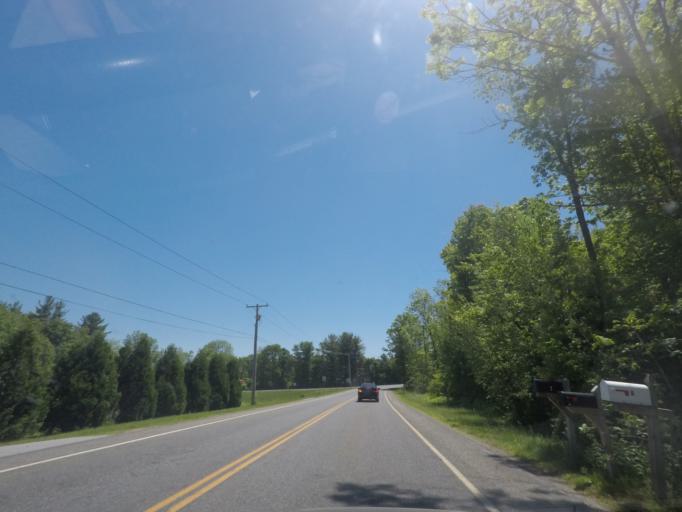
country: US
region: New York
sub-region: Saratoga County
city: Mechanicville
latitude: 42.9453
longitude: -73.7100
